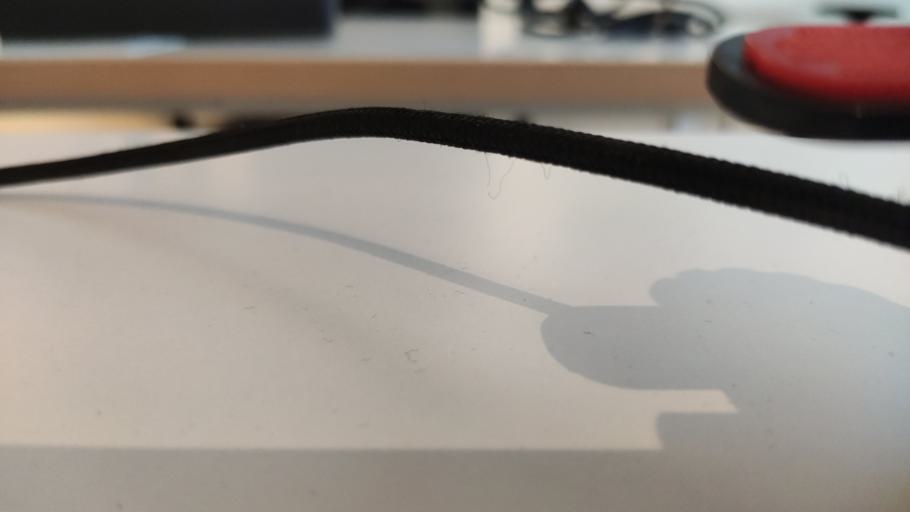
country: RU
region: Moskovskaya
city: Novopetrovskoye
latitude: 55.9527
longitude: 36.4381
